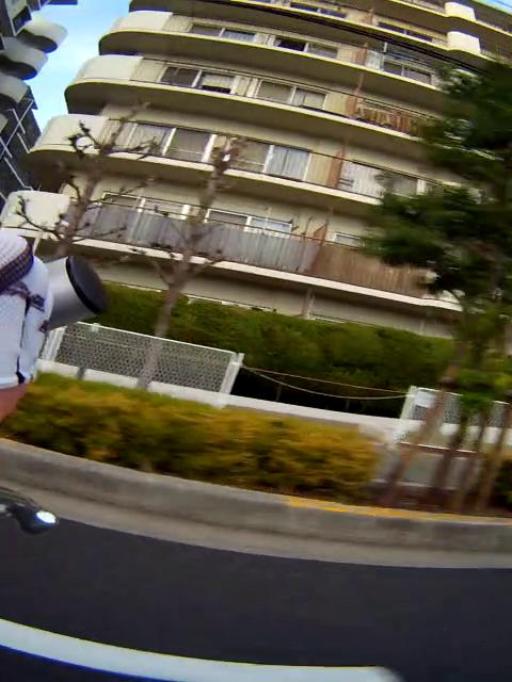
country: JP
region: Hyogo
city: Amagasaki
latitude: 34.7319
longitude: 135.4494
